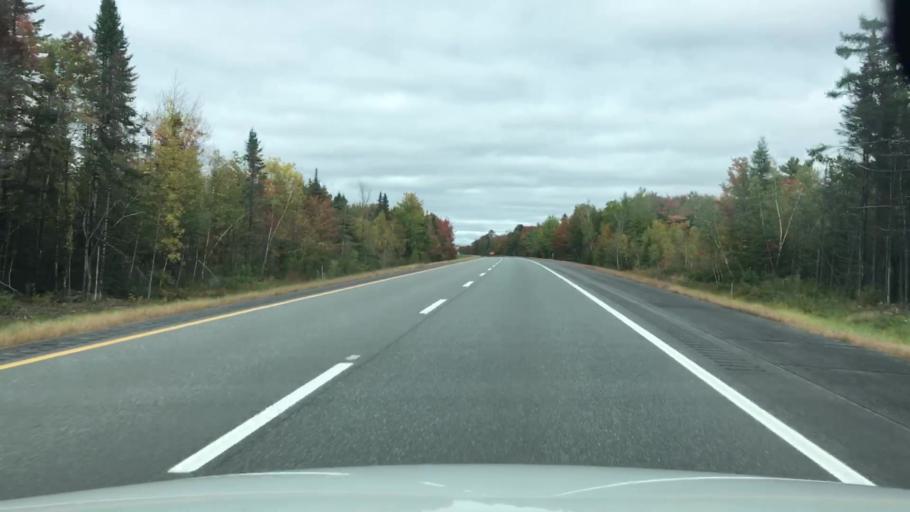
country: US
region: Maine
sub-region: Waldo County
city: Burnham
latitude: 44.7116
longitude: -69.4488
